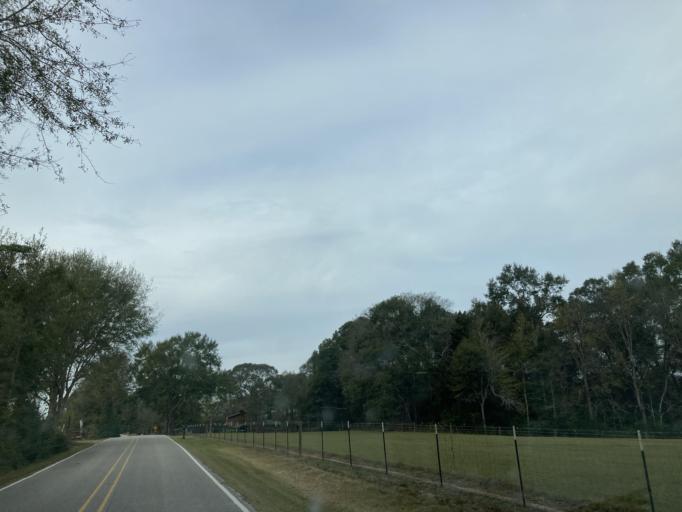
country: US
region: Mississippi
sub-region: Lamar County
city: Purvis
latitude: 31.1110
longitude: -89.4742
